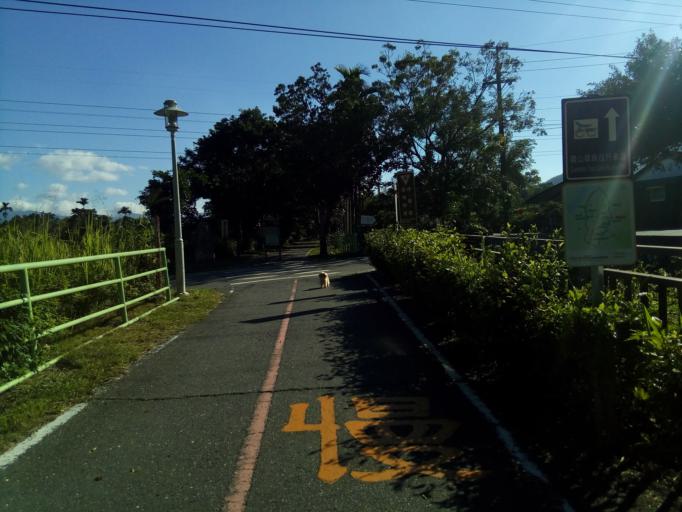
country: TW
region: Taiwan
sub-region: Taitung
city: Taitung
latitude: 23.0468
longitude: 121.1533
